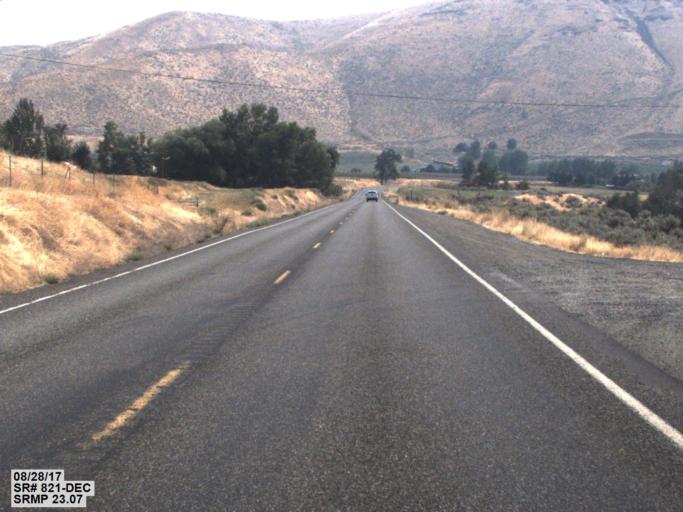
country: US
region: Washington
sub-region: Kittitas County
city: Ellensburg
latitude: 46.9062
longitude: -120.4981
